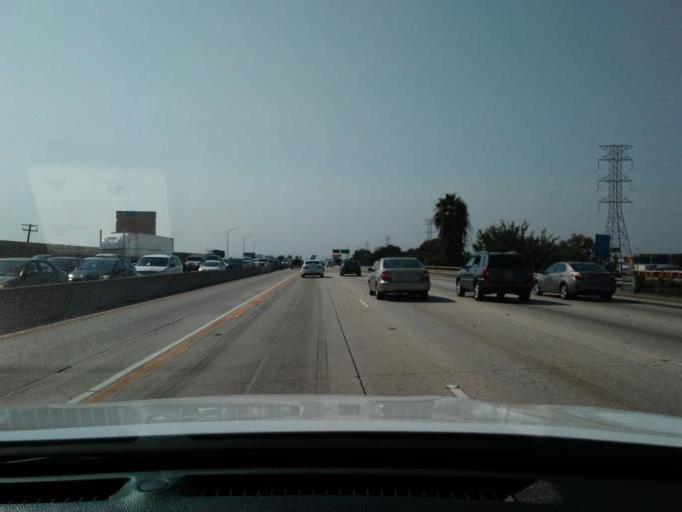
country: US
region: California
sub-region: Los Angeles County
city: Carson
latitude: 33.8348
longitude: -118.2587
